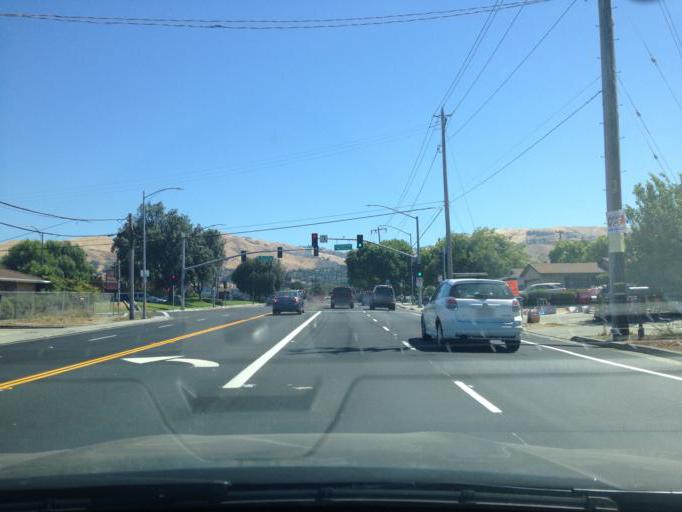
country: US
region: California
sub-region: Santa Clara County
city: Alum Rock
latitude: 37.3734
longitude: -121.8381
